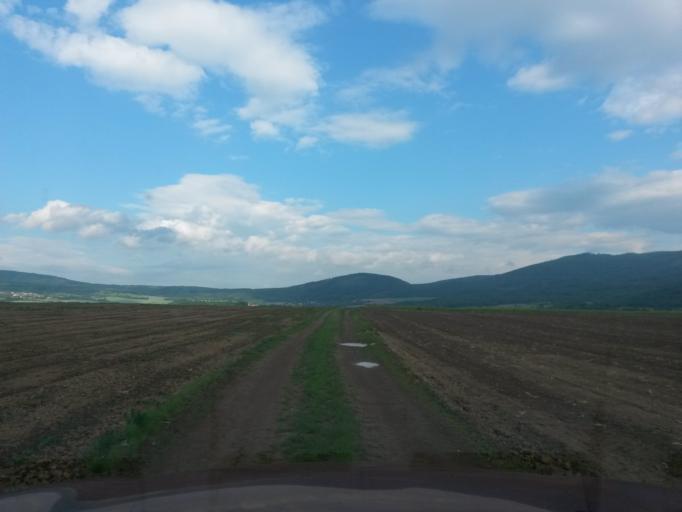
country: SK
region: Kosicky
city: Kosice
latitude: 48.7467
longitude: 21.4605
